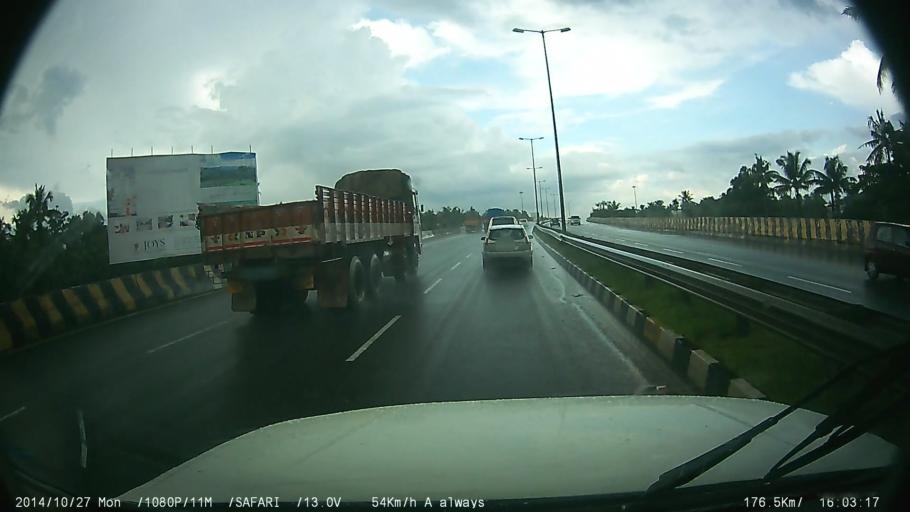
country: IN
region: Kerala
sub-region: Thrissur District
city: Kizhake Chalakudi
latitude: 10.3263
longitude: 76.3230
